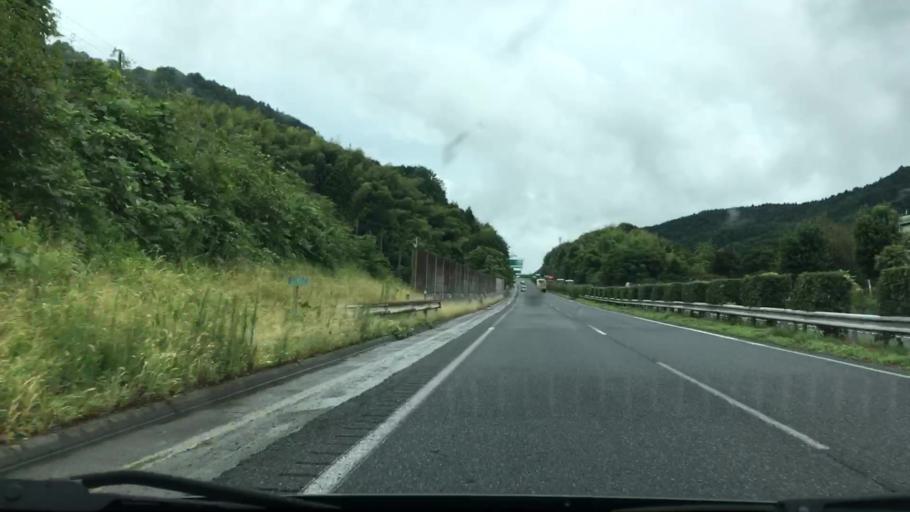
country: JP
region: Hyogo
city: Yamazakicho-nakabirose
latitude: 34.9732
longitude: 134.6559
